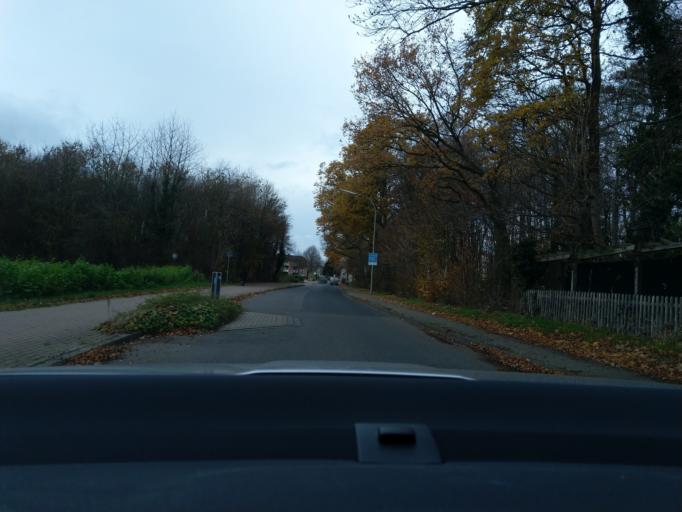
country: DE
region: North Rhine-Westphalia
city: Wegberg
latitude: 51.1385
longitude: 6.3010
